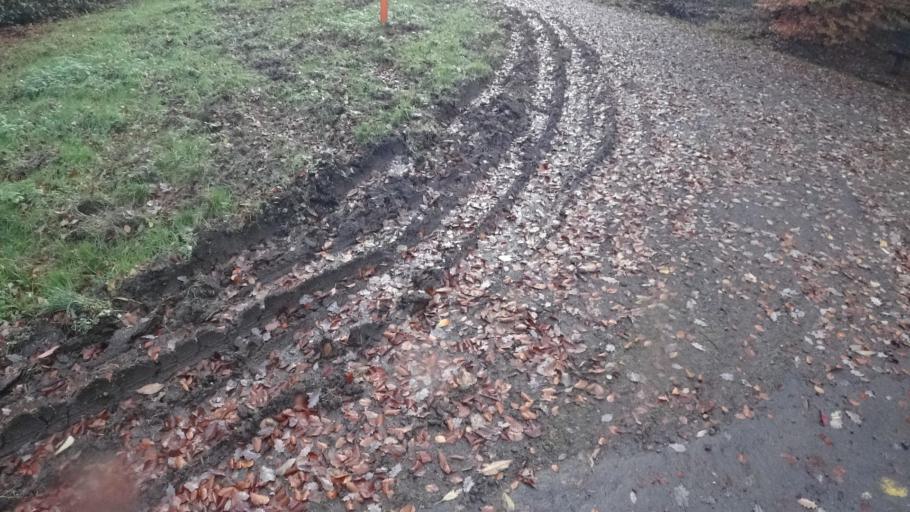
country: DE
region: Rheinland-Pfalz
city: Gondershausen
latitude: 50.1473
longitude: 7.5049
